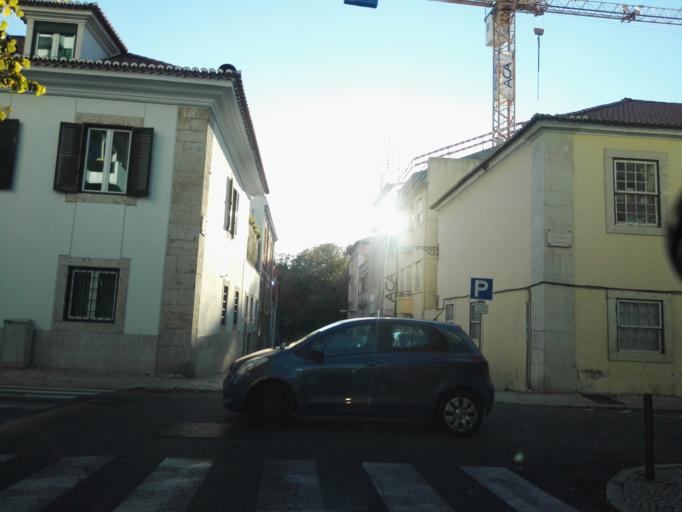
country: PT
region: Lisbon
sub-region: Lisbon
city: Lisbon
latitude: 38.7228
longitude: -9.1554
